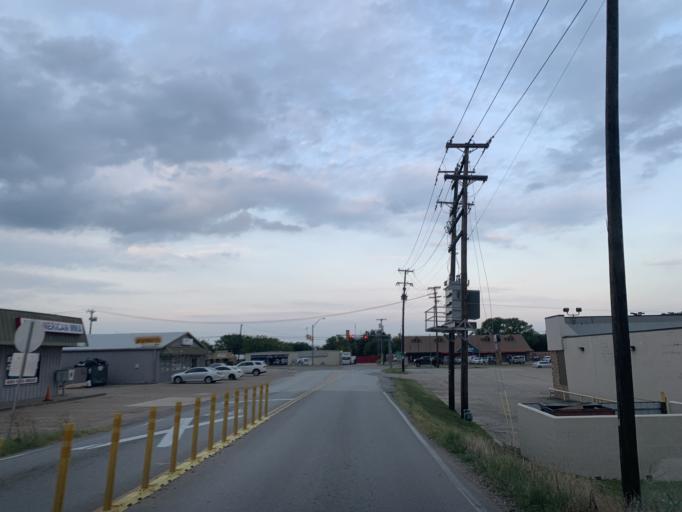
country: US
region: Texas
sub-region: Tarrant County
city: Keller
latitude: 32.9387
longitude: -97.2547
